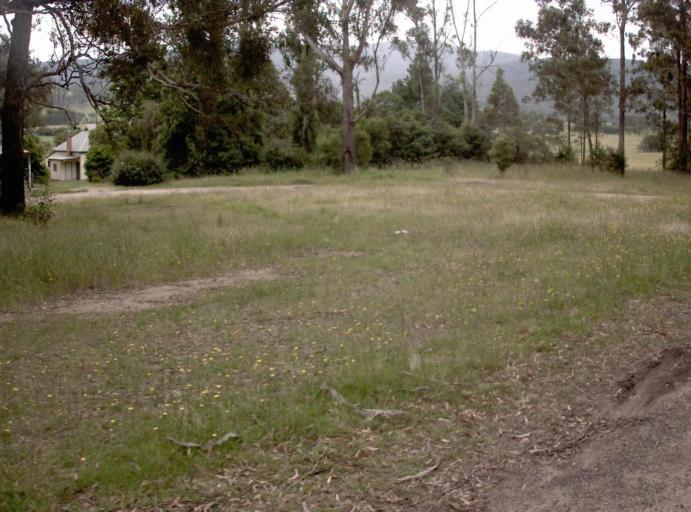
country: AU
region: New South Wales
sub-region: Bombala
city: Bombala
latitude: -37.4980
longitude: 149.1810
